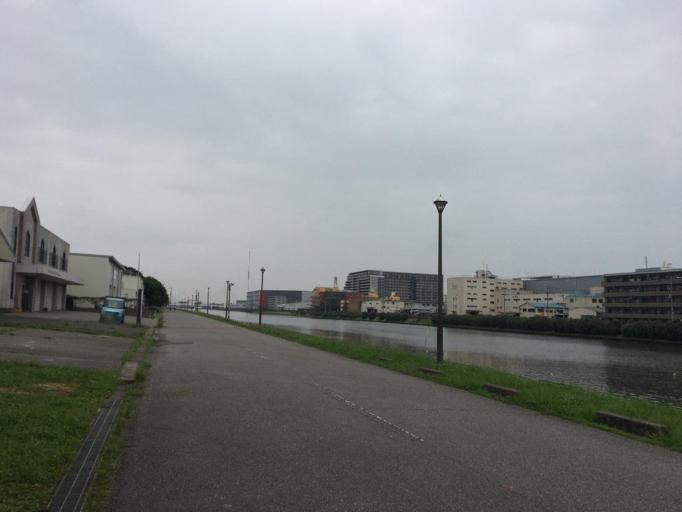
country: JP
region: Saitama
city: Shimotoda
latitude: 35.8022
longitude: 139.6743
